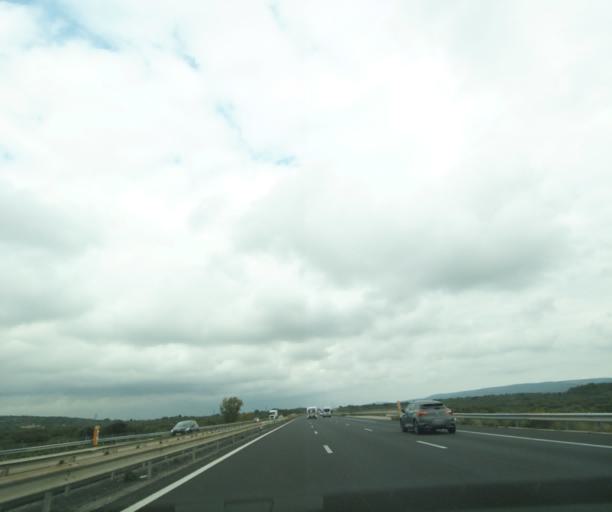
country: FR
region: Languedoc-Roussillon
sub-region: Departement de l'Herault
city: Bouzigues
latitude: 43.4694
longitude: 3.6396
